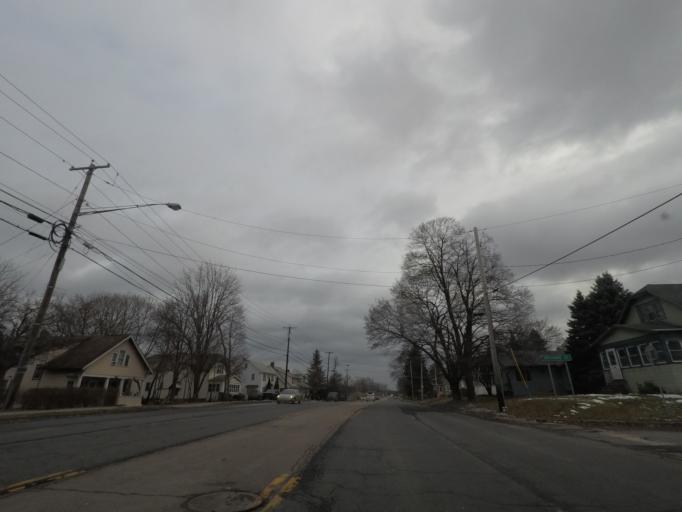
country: US
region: New York
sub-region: Rensselaer County
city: Hampton Manor
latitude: 42.6168
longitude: -73.7315
